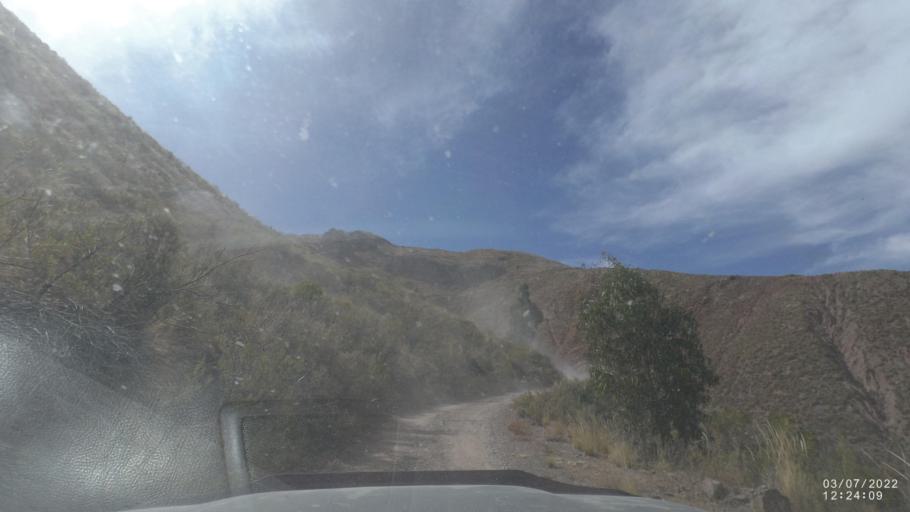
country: BO
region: Cochabamba
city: Irpa Irpa
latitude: -17.8138
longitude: -66.6178
